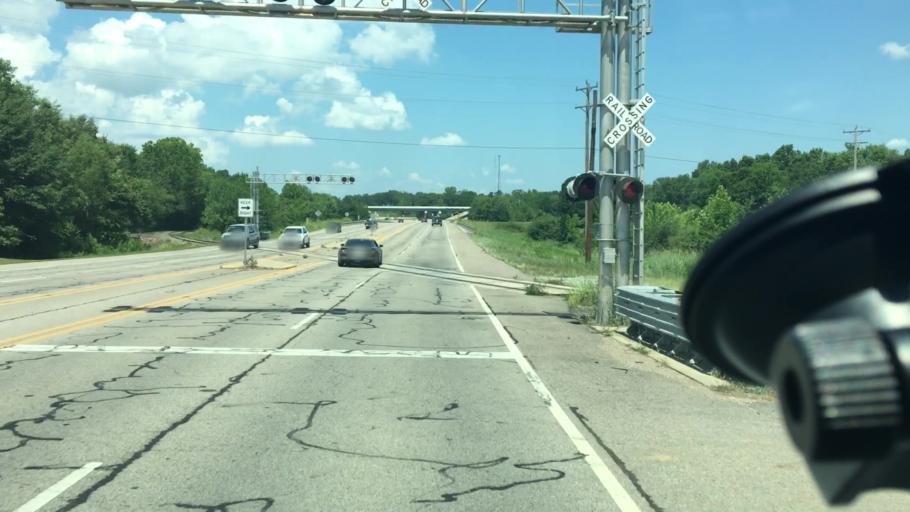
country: US
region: Arkansas
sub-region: Sebastian County
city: Barling
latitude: 35.3188
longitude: -94.2875
